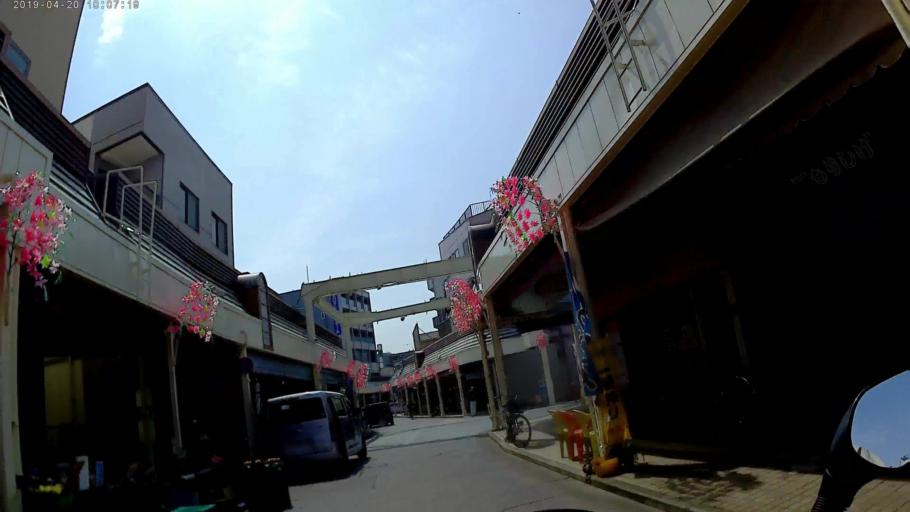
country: JP
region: Kanagawa
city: Yokohama
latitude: 35.4890
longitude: 139.6453
